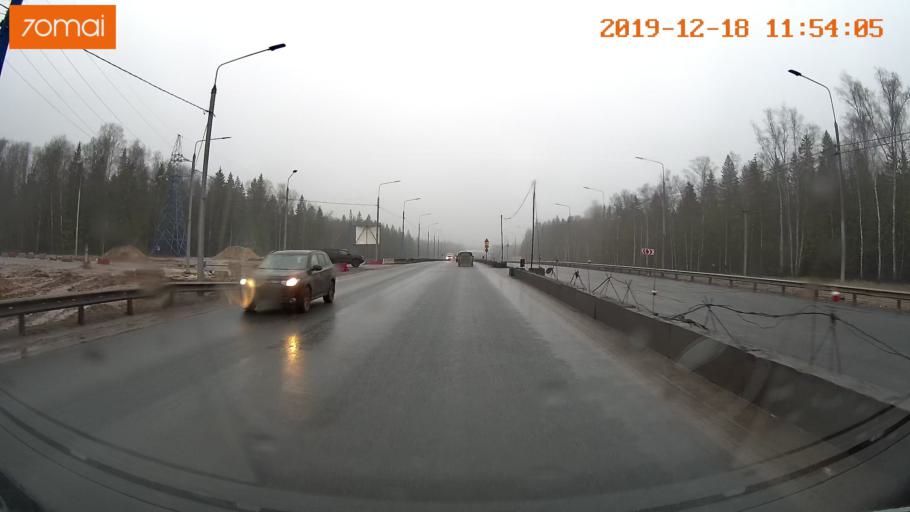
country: RU
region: Moskovskaya
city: Yershovo
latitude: 55.8118
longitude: 36.9188
